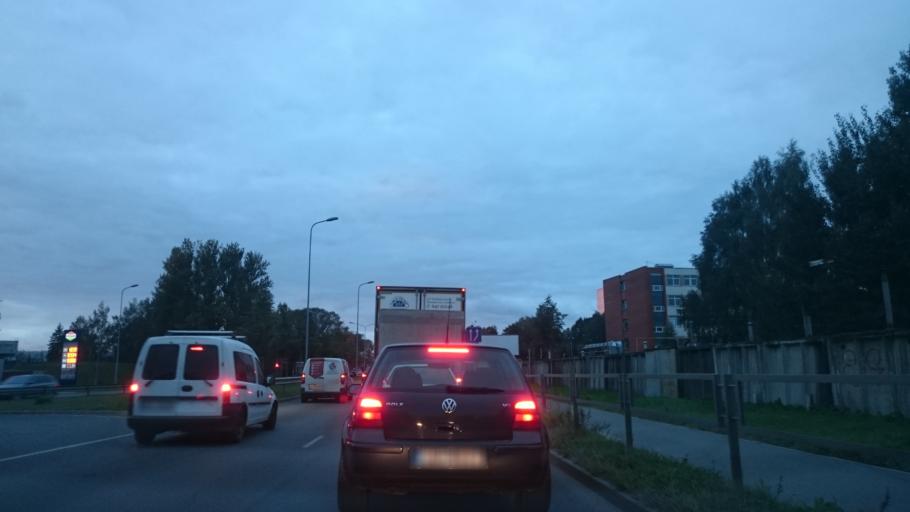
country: LV
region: Kekava
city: Balozi
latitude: 56.9248
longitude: 24.1888
